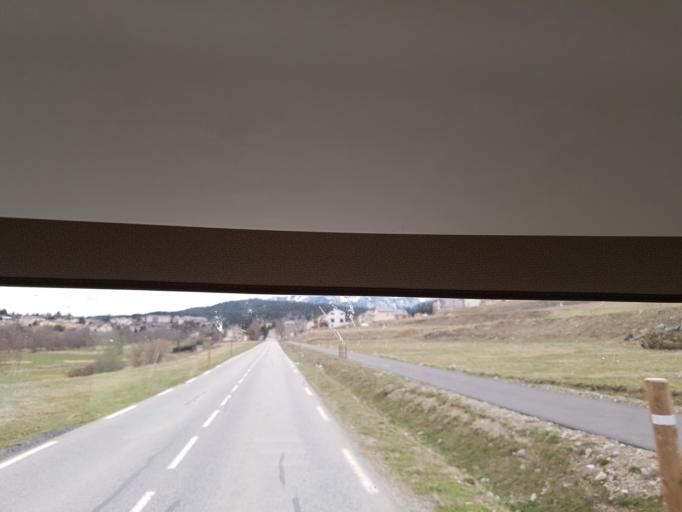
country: ES
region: Catalonia
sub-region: Provincia de Girona
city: Llivia
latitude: 42.6201
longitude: 2.1095
